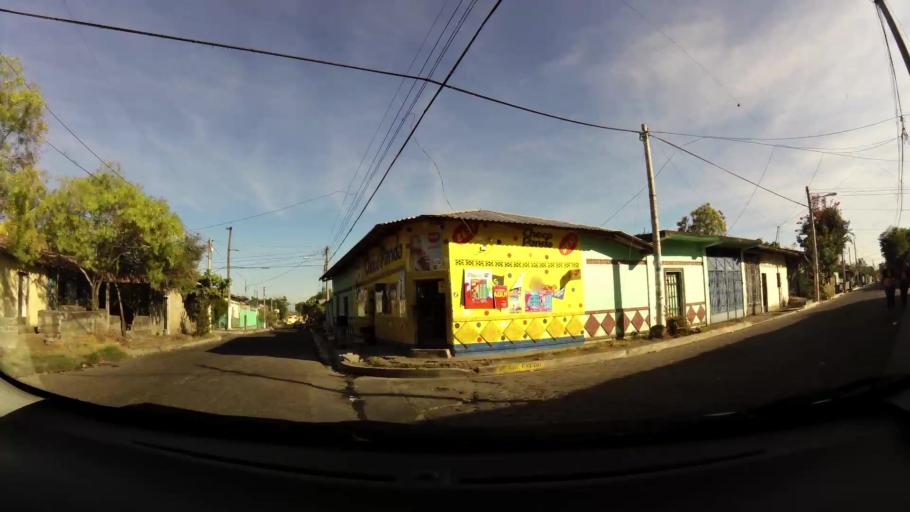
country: SV
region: San Miguel
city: San Miguel
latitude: 13.4680
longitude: -88.1851
